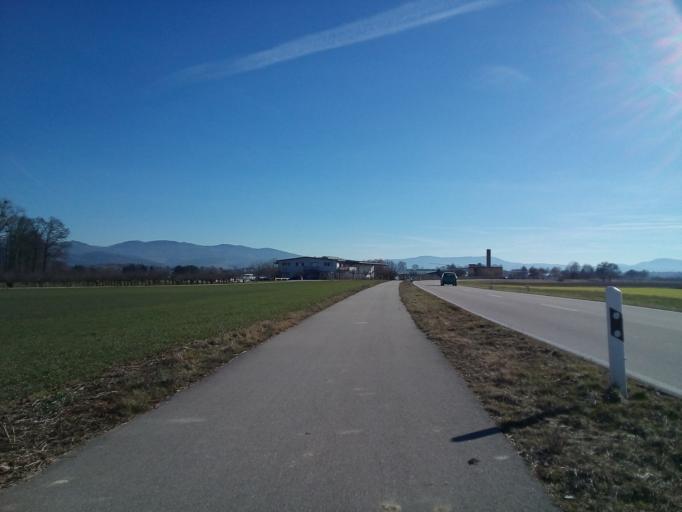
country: DE
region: Baden-Wuerttemberg
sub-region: Freiburg Region
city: Renchen
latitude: 48.6187
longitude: 8.0180
